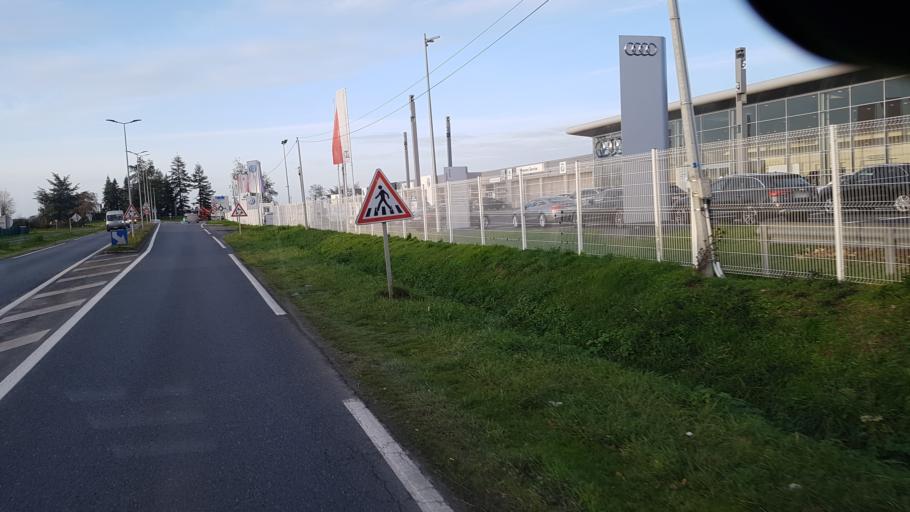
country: FR
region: Centre
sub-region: Departement de l'Indre
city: Chateauroux
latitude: 46.7928
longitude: 1.7149
